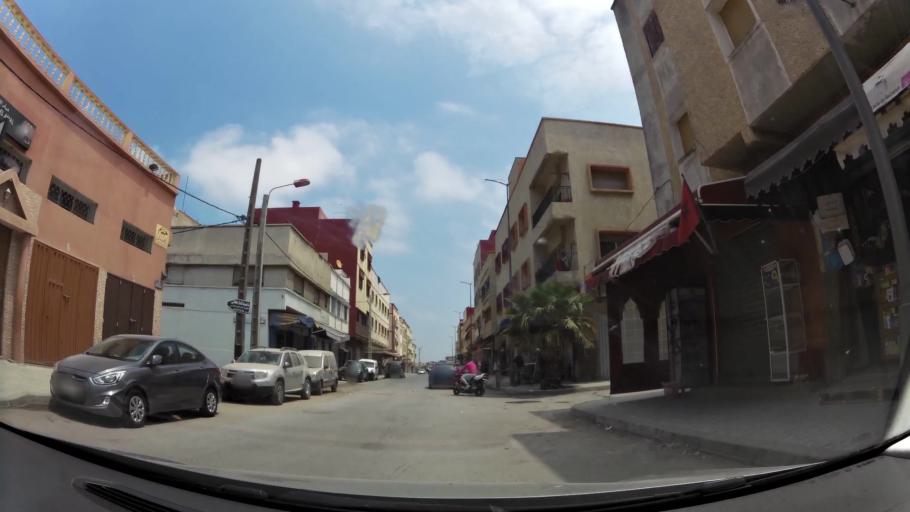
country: MA
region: Rabat-Sale-Zemmour-Zaer
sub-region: Rabat
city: Rabat
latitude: 33.9876
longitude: -6.8815
